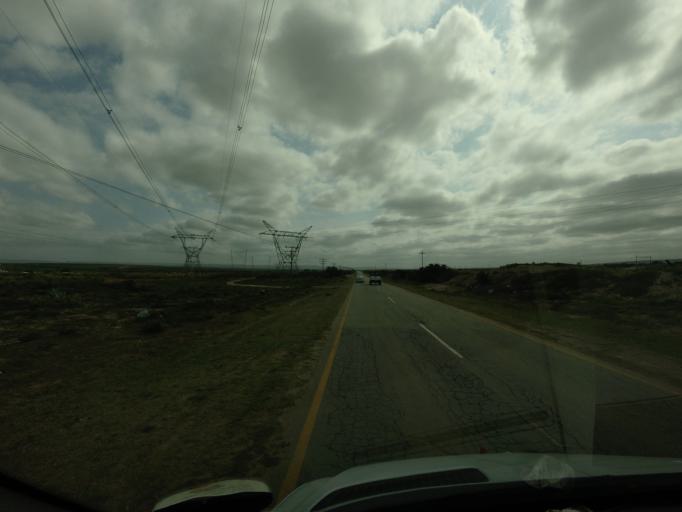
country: ZA
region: Eastern Cape
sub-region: Cacadu District Municipality
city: Kirkwood
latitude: -33.5034
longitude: 25.6950
